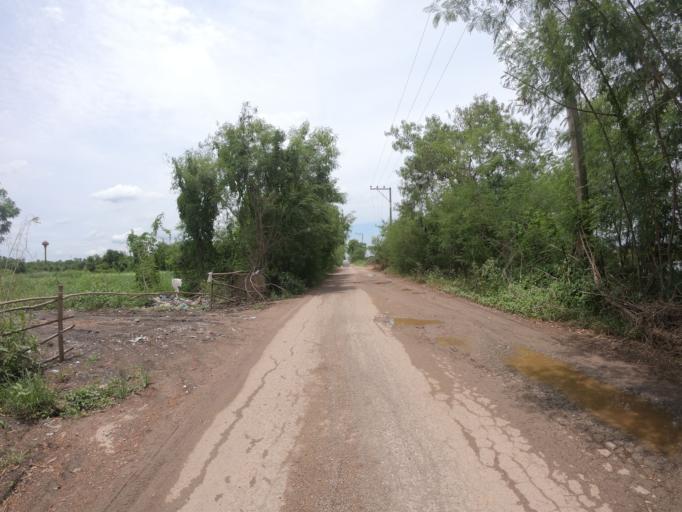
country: TH
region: Pathum Thani
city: Ban Lam Luk Ka
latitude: 13.9861
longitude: 100.8482
